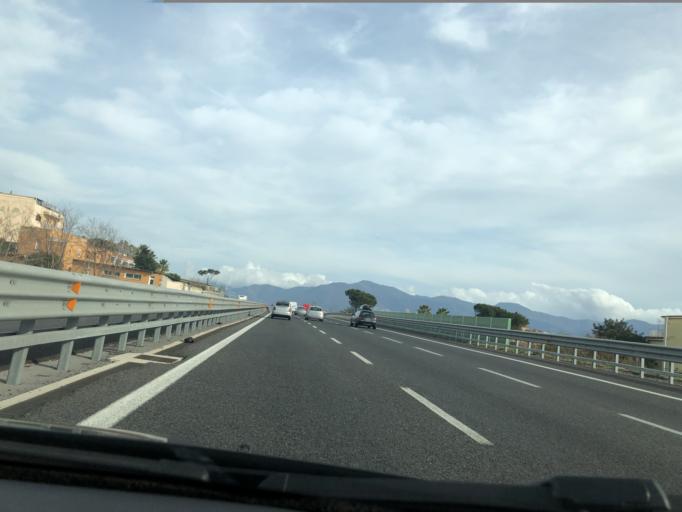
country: IT
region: Campania
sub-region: Provincia di Napoli
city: Trecase
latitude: 40.7651
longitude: 14.4336
